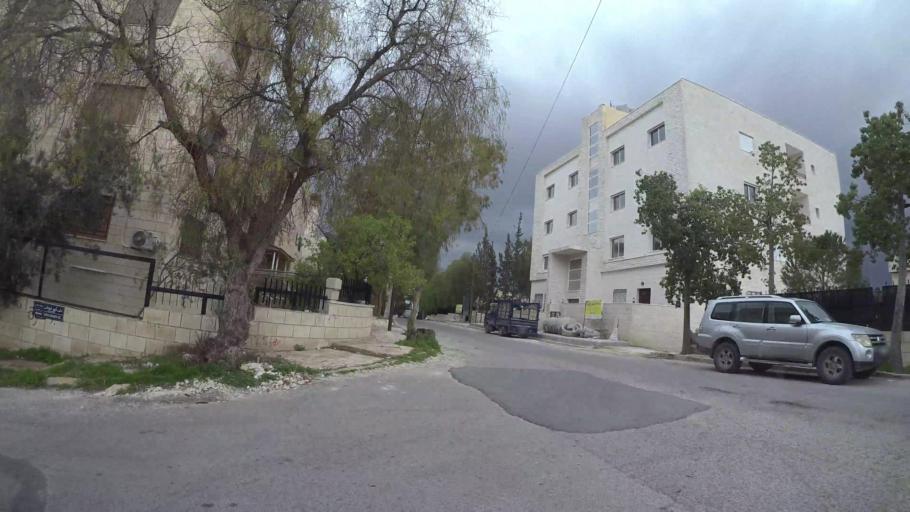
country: JO
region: Amman
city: Amman
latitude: 32.0047
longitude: 35.9465
